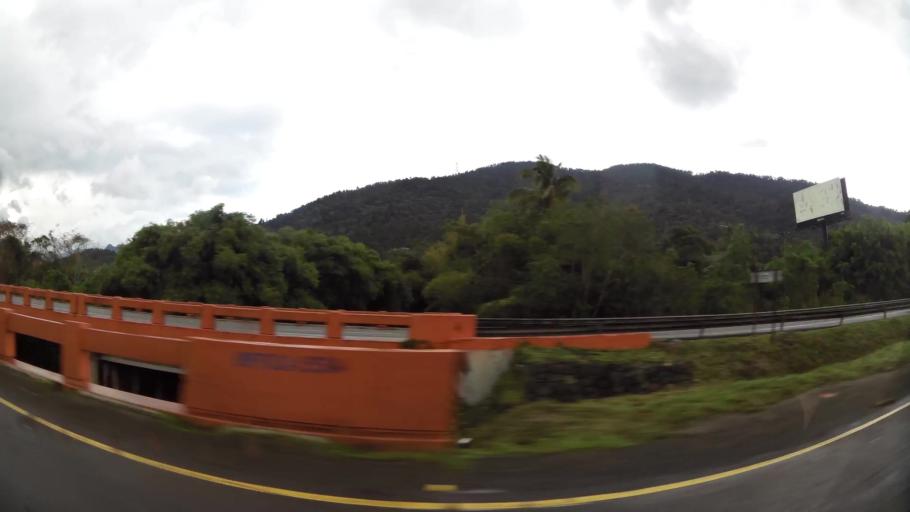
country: DO
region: San Cristobal
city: Villa Altagracia
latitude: 18.7062
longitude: -70.1969
